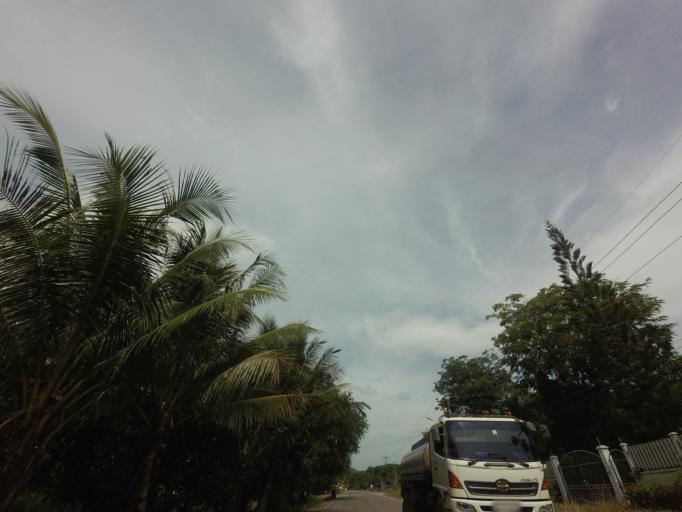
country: TH
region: Rayong
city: Klaeng
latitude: 12.6770
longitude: 101.5533
